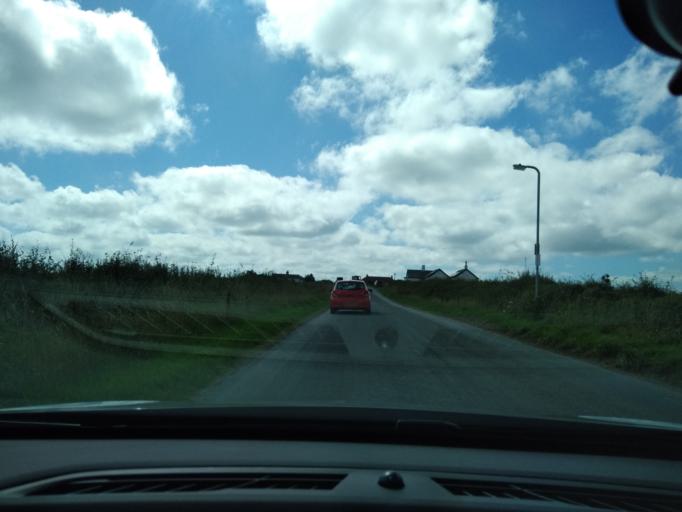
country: GB
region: England
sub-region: Cumbria
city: Millom
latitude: 54.2210
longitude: -3.3436
